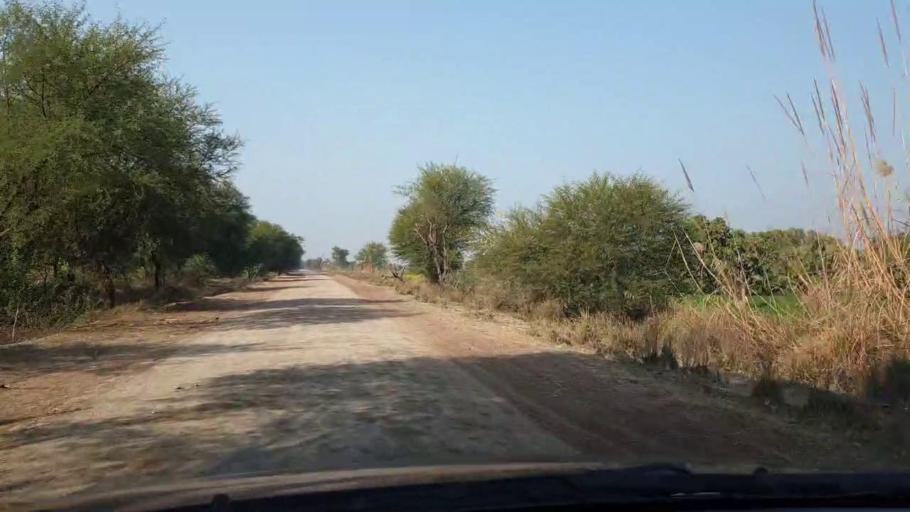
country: PK
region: Sindh
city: Jhol
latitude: 25.9613
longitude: 68.9702
